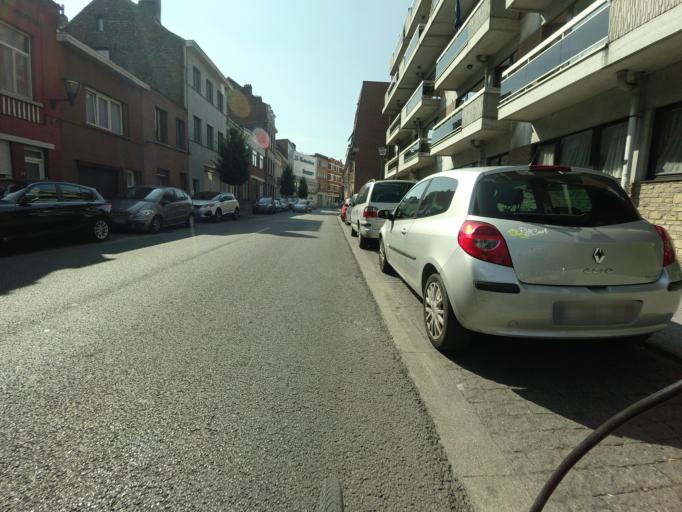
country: BE
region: Brussels Capital
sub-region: Bruxelles-Capitale
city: Brussels
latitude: 50.8580
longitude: 4.3311
